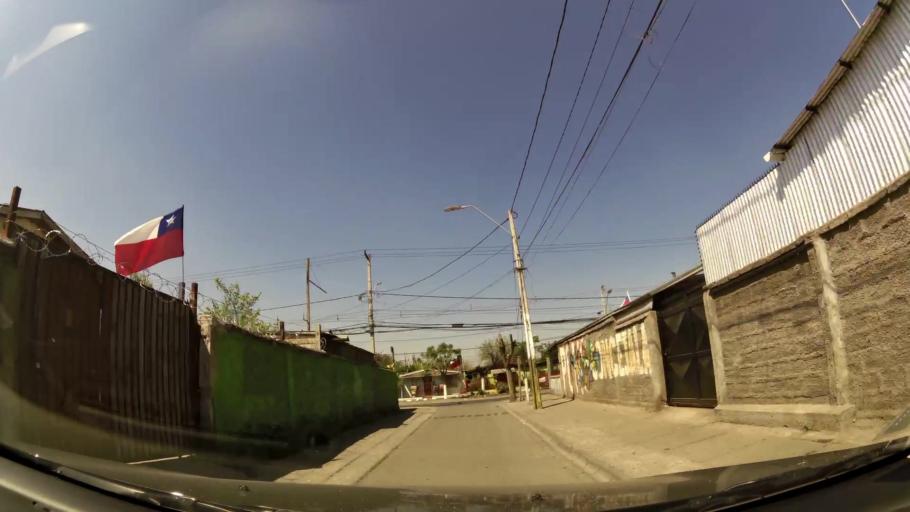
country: CL
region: Santiago Metropolitan
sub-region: Provincia de Maipo
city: San Bernardo
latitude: -33.5787
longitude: -70.7038
